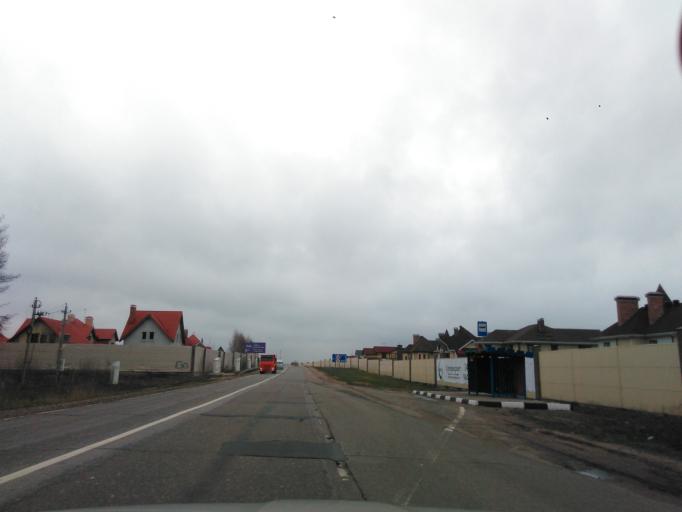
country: RU
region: Moskovskaya
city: Rozhdestveno
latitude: 55.8248
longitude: 37.0435
